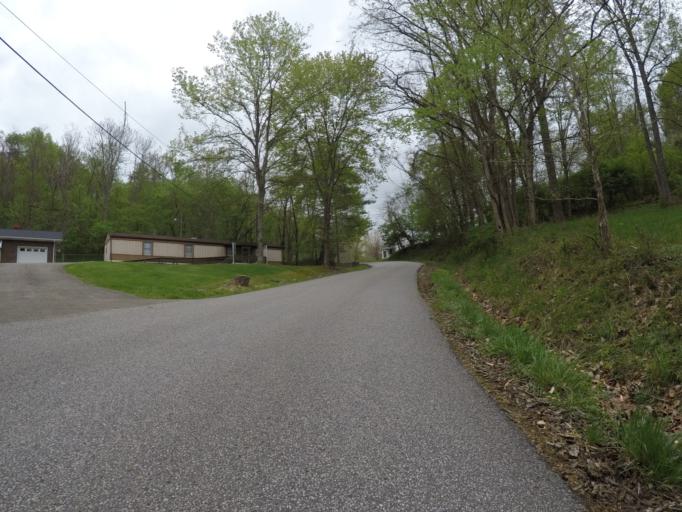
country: US
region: West Virginia
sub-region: Cabell County
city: Barboursville
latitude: 38.4042
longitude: -82.2775
